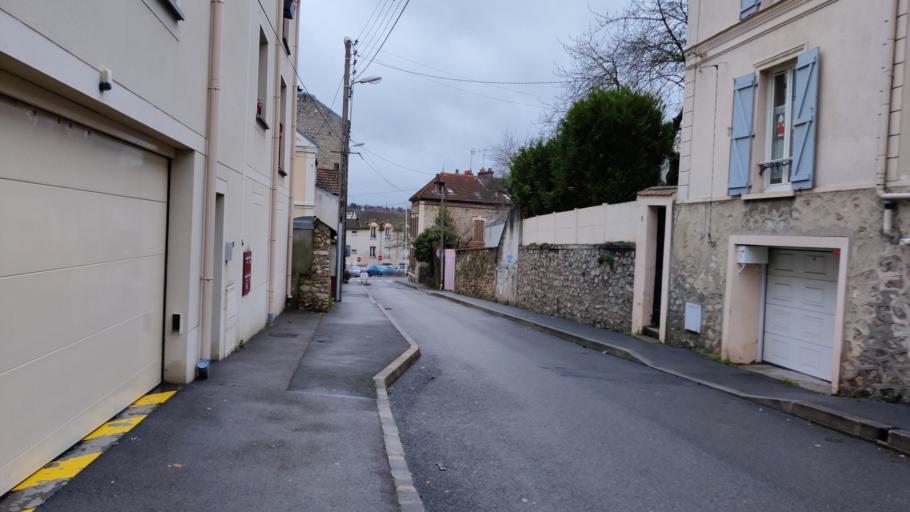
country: FR
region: Ile-de-France
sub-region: Departement de Seine-et-Marne
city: Thorigny-sur-Marne
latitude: 48.8851
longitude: 2.7145
